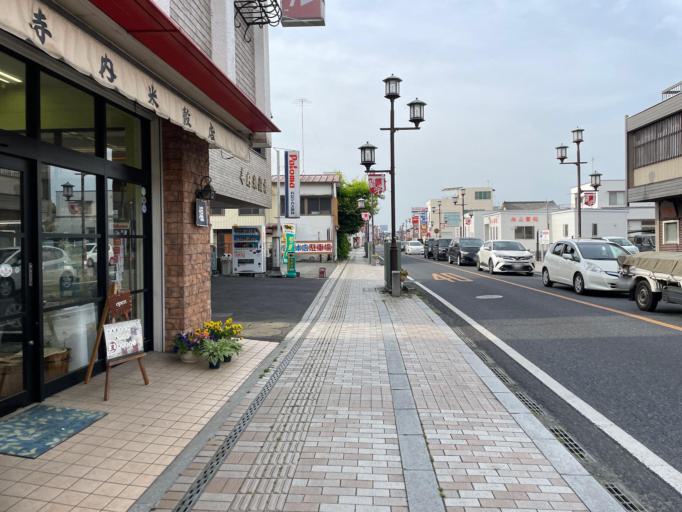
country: JP
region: Tochigi
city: Mibu
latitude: 36.4241
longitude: 139.8028
